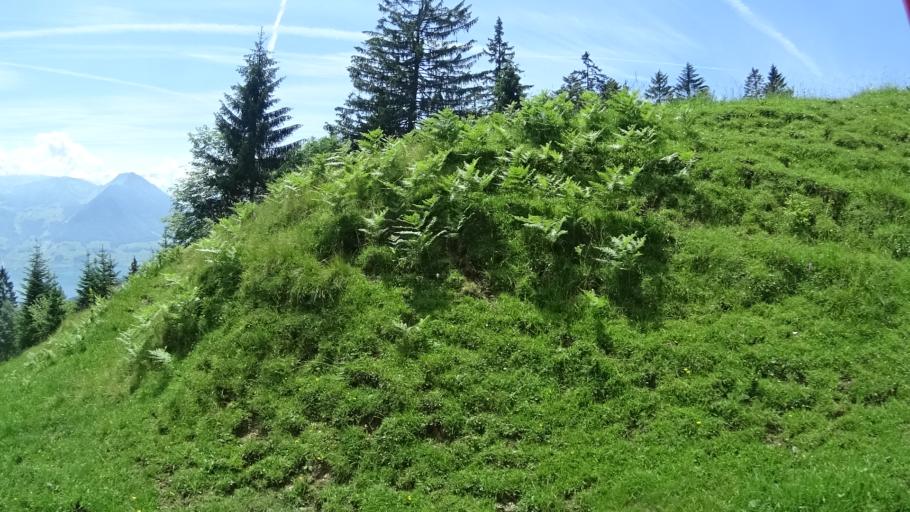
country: CH
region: Lucerne
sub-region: Lucerne-Land District
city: Vitznau
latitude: 47.0381
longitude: 8.4739
